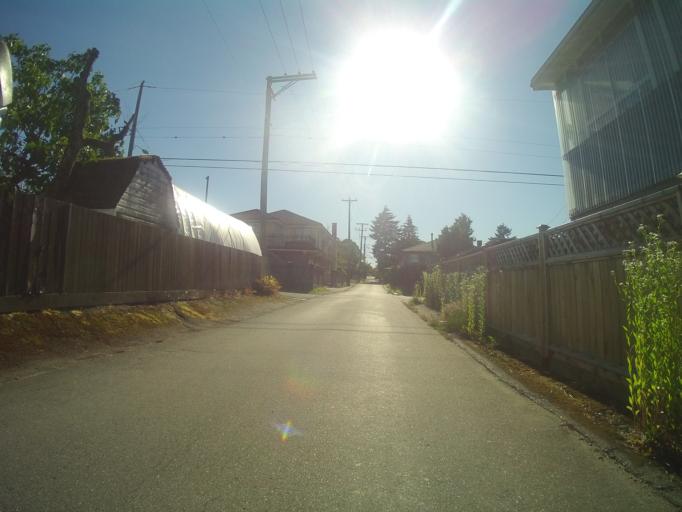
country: CA
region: British Columbia
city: Vancouver
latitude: 49.2430
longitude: -123.0684
